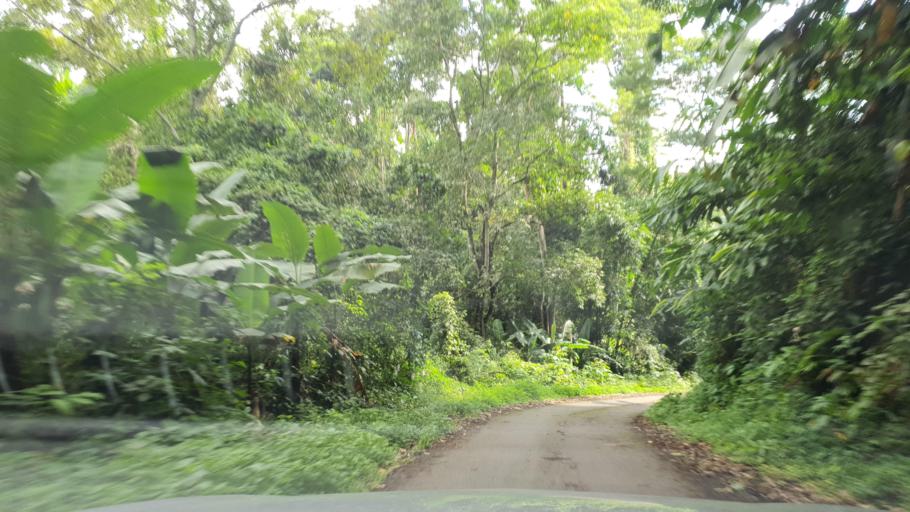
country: TH
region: Chiang Mai
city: Mae On
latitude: 18.9410
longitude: 99.3098
